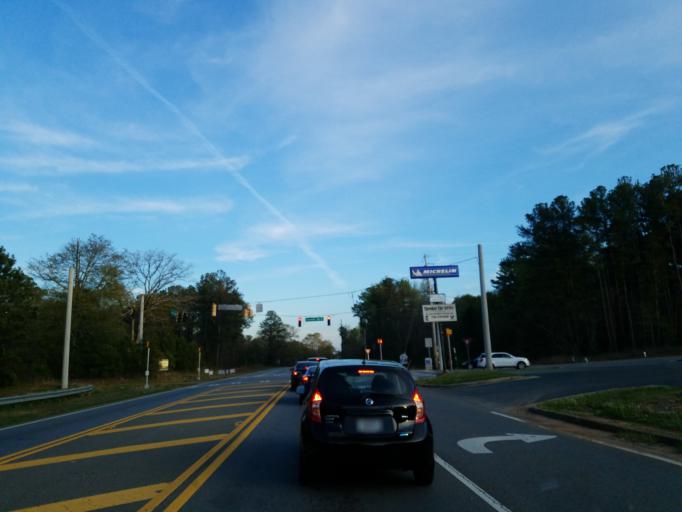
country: US
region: Georgia
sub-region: Cherokee County
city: Canton
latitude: 34.2022
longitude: -84.4538
